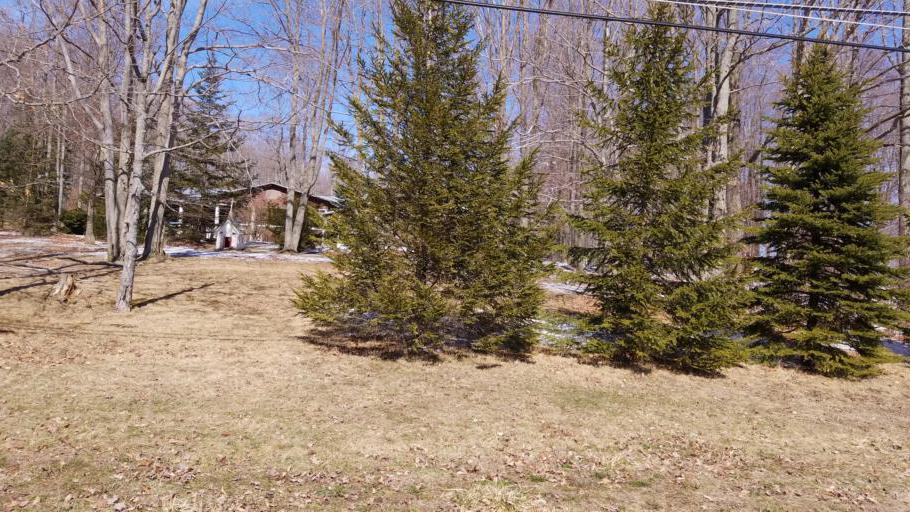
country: US
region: Pennsylvania
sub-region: Potter County
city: Galeton
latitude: 41.9013
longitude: -77.7517
